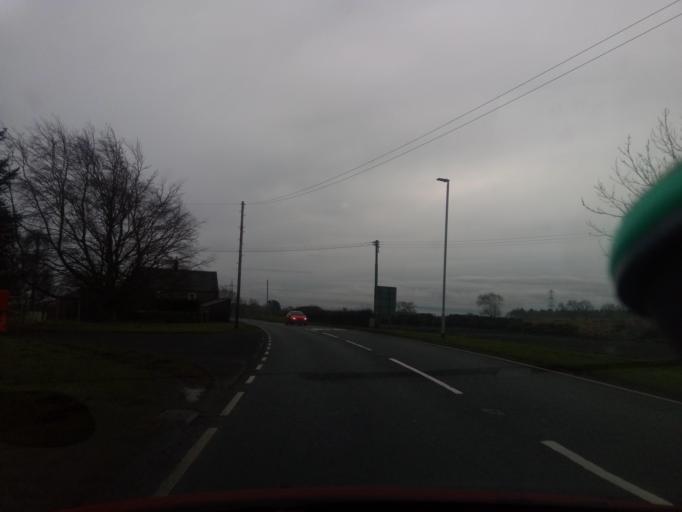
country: GB
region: England
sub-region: Northumberland
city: Corbridge
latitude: 55.0125
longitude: -2.0212
